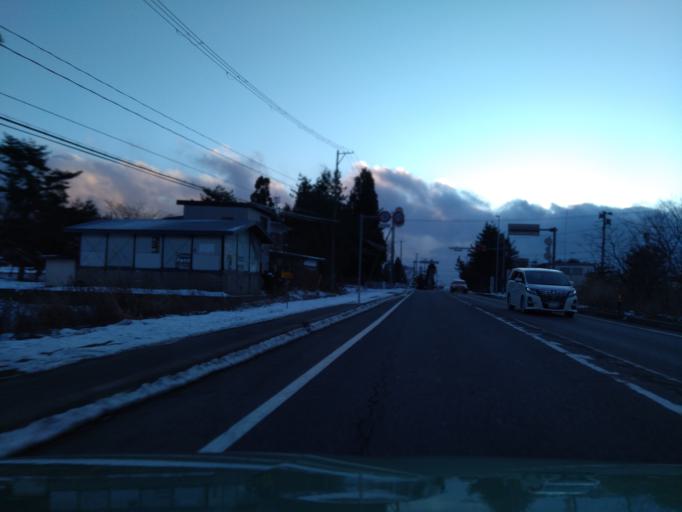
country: JP
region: Iwate
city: Shizukuishi
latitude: 39.6962
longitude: 141.0202
